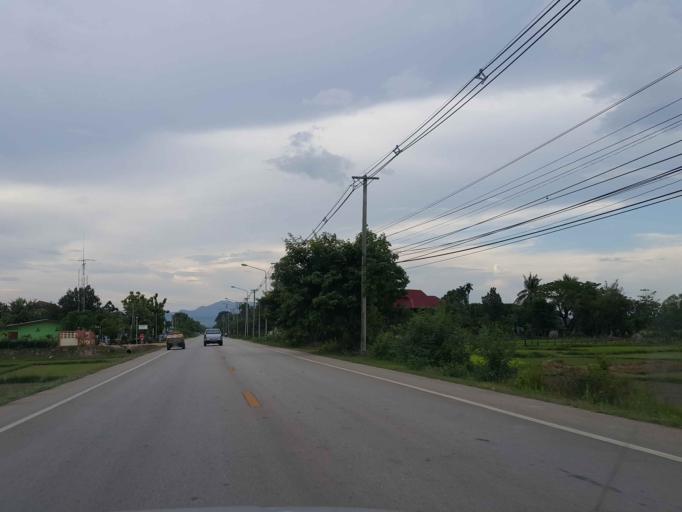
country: TH
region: Lampang
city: Hang Chat
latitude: 18.2852
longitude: 99.3795
